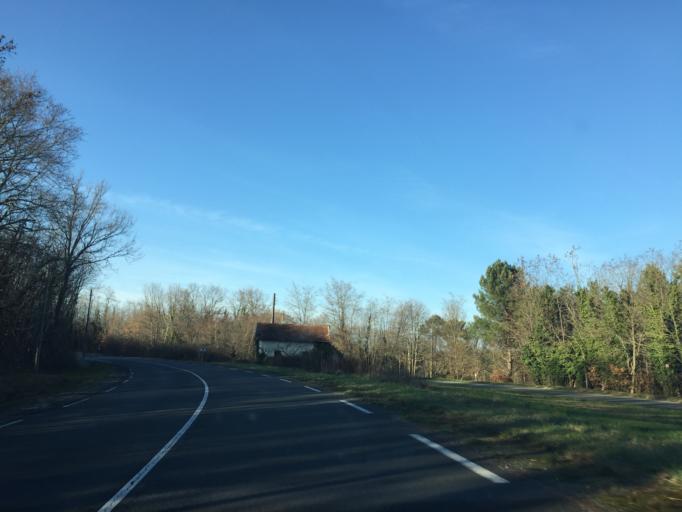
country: FR
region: Aquitaine
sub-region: Departement de la Dordogne
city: Riberac
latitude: 45.1904
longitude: 0.3754
